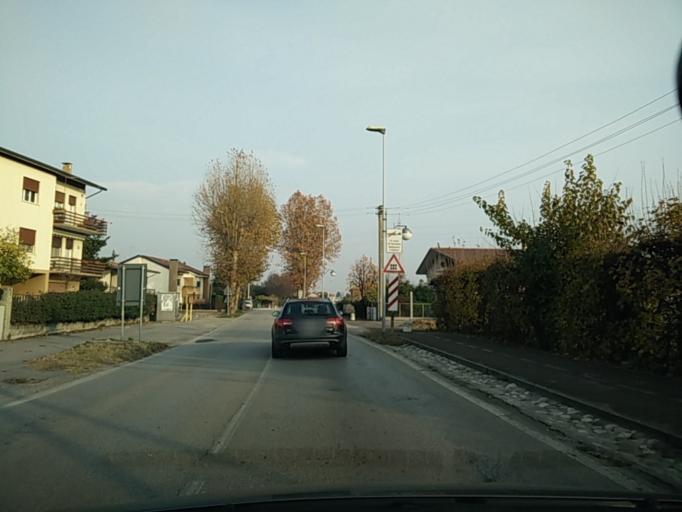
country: IT
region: Veneto
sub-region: Provincia di Treviso
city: Castelfranco Veneto
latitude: 45.6732
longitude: 11.9512
